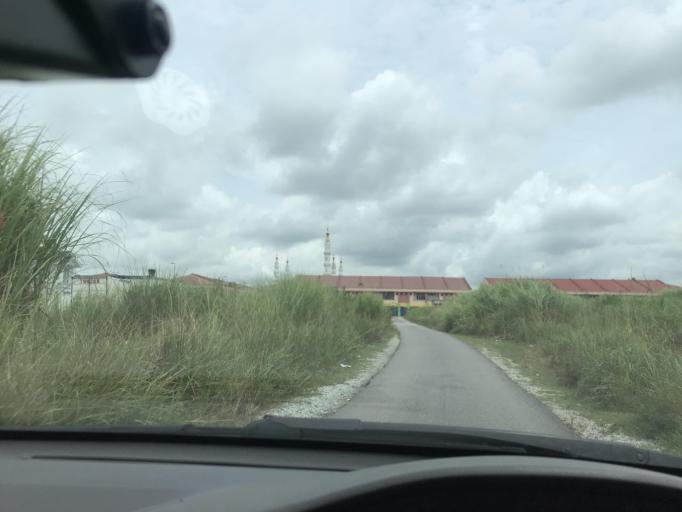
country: MY
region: Kelantan
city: Kota Bharu
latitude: 6.1196
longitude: 102.2194
